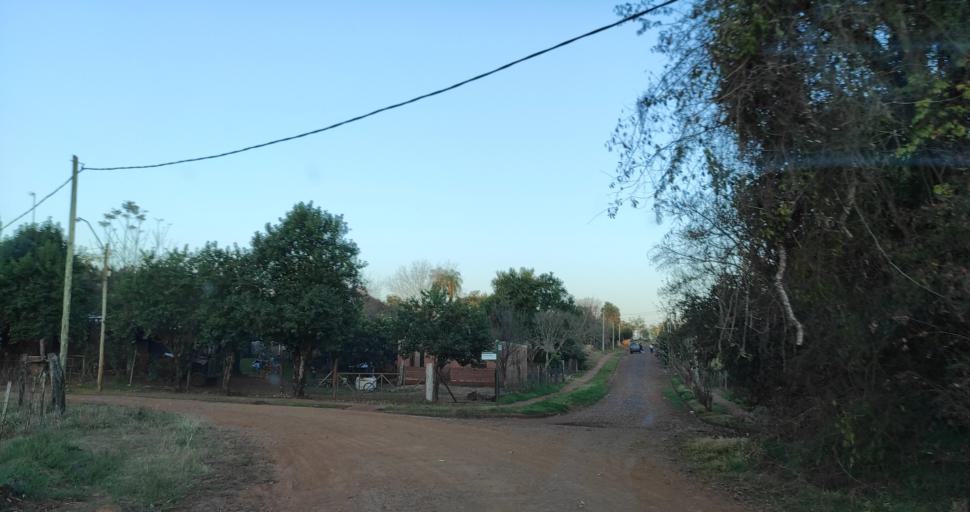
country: AR
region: Misiones
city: Capiovi
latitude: -26.8916
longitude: -55.0742
